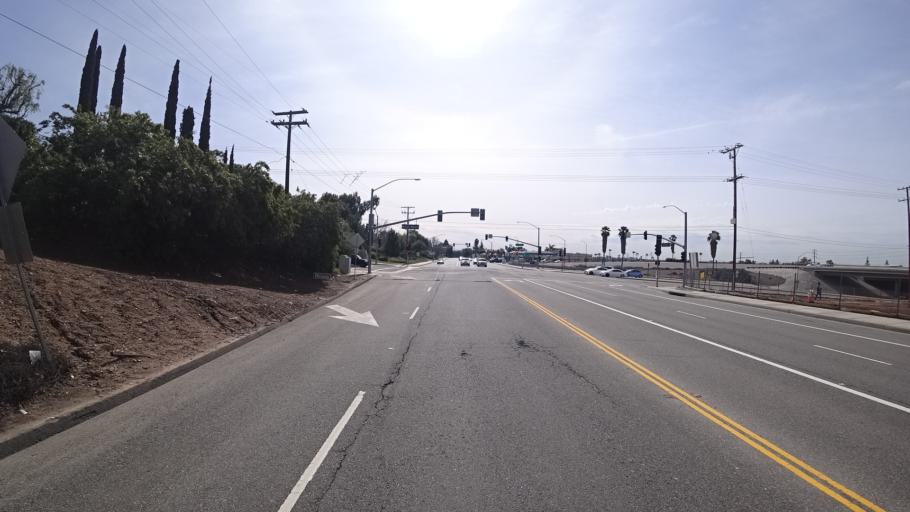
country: US
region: California
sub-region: Orange County
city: Villa Park
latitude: 33.8355
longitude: -117.8339
